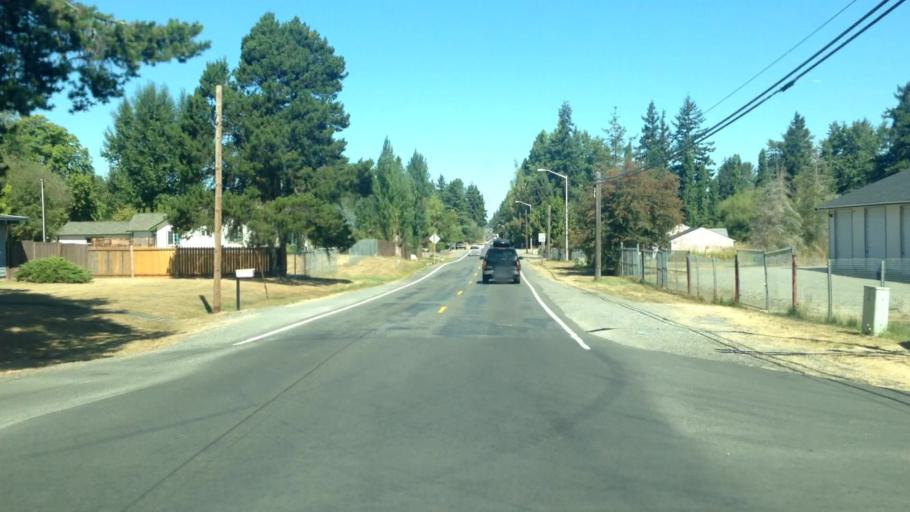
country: US
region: Washington
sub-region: Pierce County
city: Parkland
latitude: 47.1474
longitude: -122.4156
